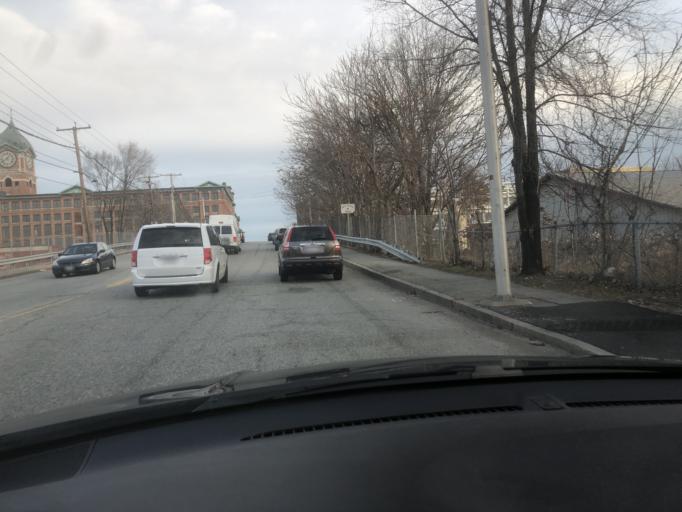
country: US
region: Massachusetts
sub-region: Essex County
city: Lawrence
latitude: 42.7007
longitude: -71.1534
